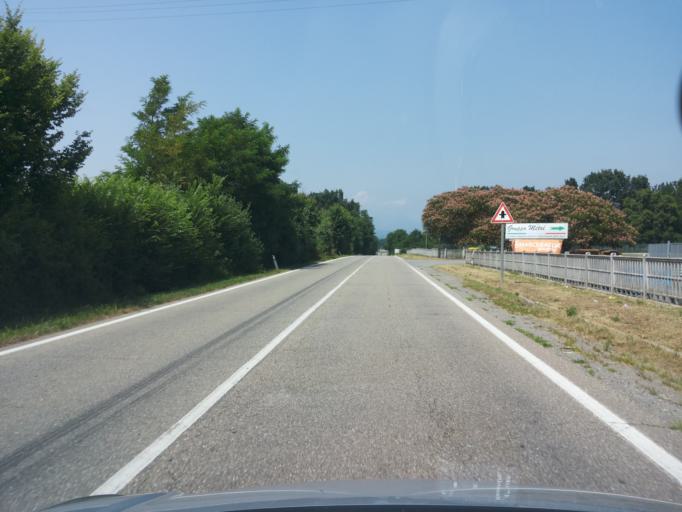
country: IT
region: Piedmont
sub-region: Provincia di Biella
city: Mottalciata
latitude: 45.4980
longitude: 8.2145
